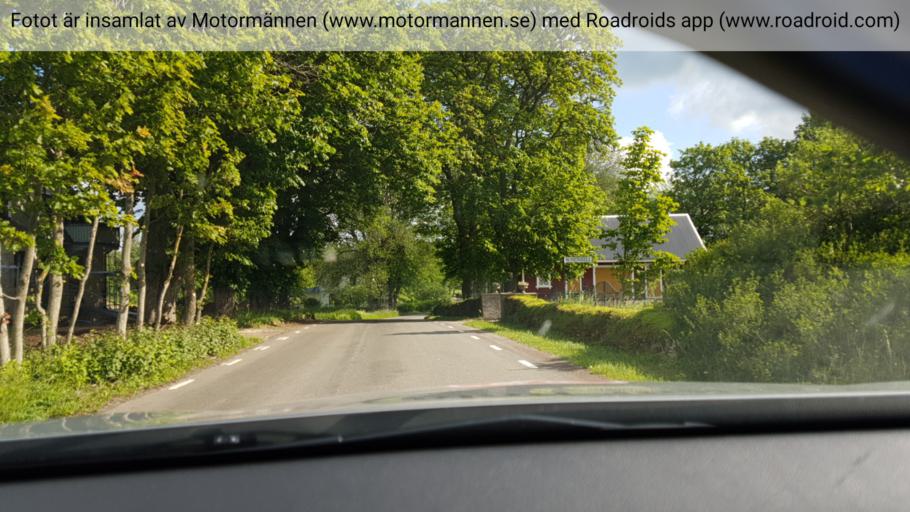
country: SE
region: Vaestra Goetaland
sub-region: Skara Kommun
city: Axvall
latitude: 58.3744
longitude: 13.6405
